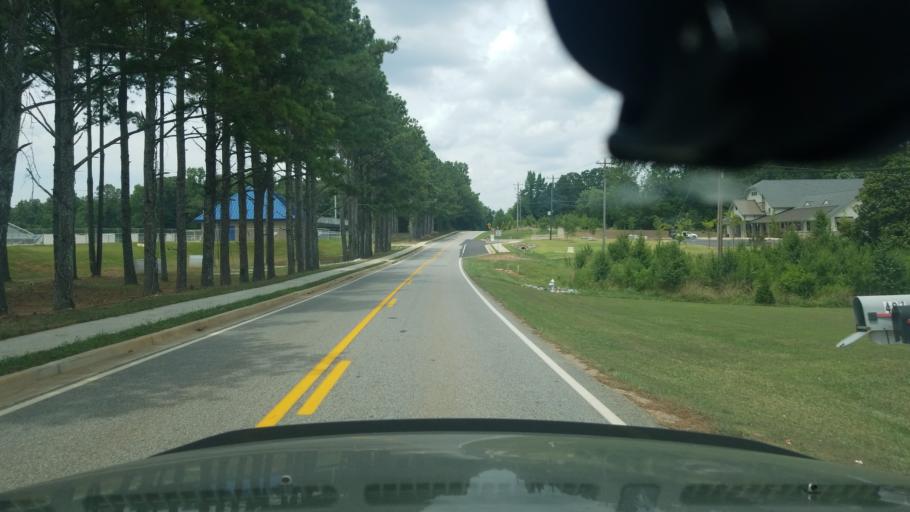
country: US
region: Georgia
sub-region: Fulton County
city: Milton
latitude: 34.1468
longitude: -84.2249
